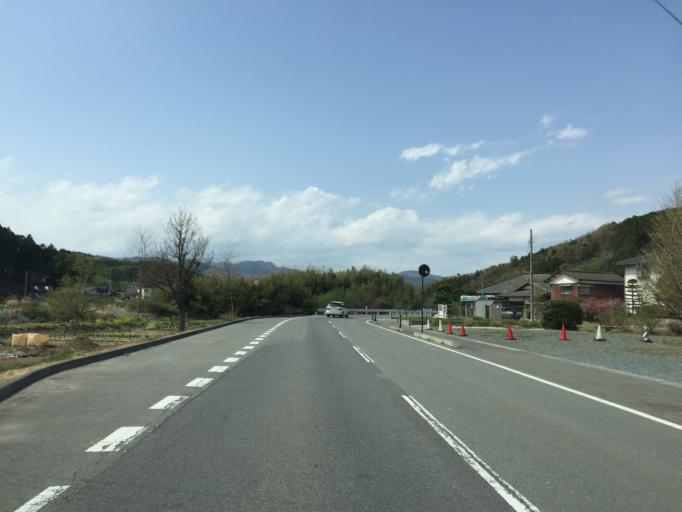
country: JP
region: Fukushima
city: Iwaki
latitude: 37.1524
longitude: 140.9850
